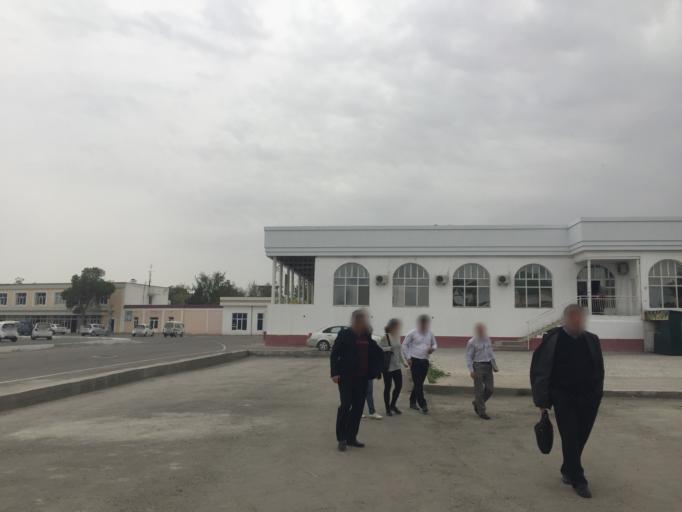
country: UZ
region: Bukhara
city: Kogon
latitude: 39.7234
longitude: 64.5467
